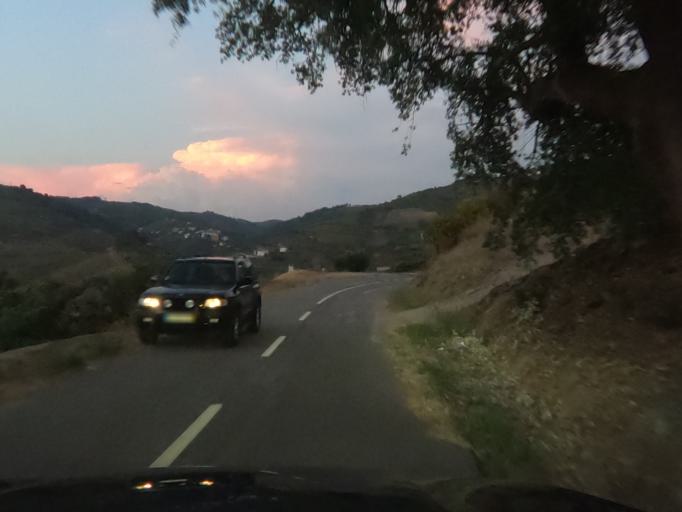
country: PT
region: Vila Real
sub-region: Santa Marta de Penaguiao
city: Santa Marta de Penaguiao
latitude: 41.2275
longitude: -7.7451
